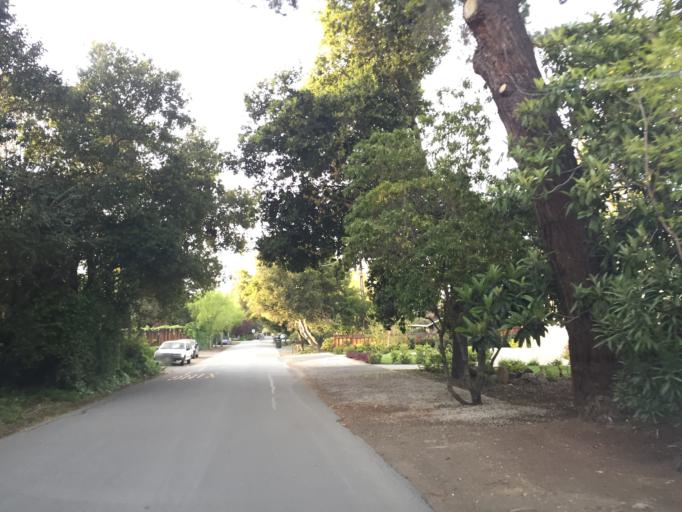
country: US
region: California
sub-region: Santa Clara County
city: Los Altos
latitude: 37.3955
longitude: -122.1225
